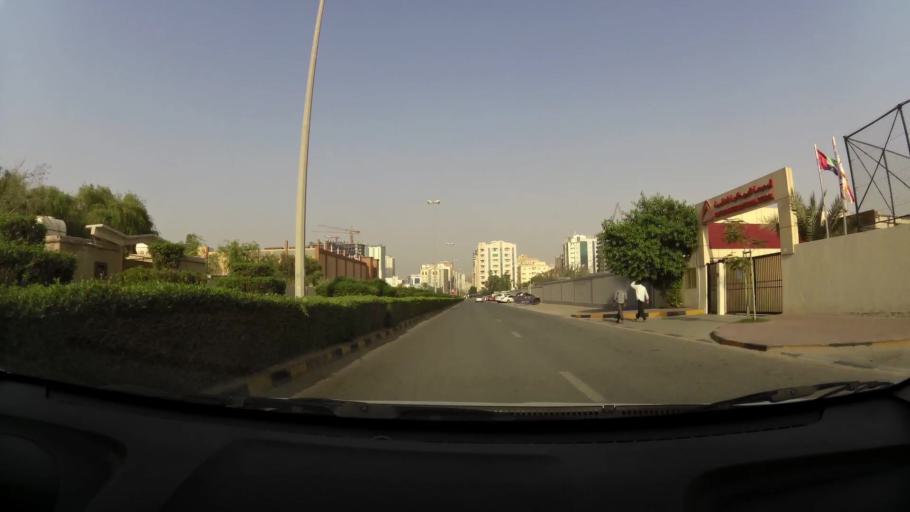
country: AE
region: Ajman
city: Ajman
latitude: 25.3895
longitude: 55.4433
